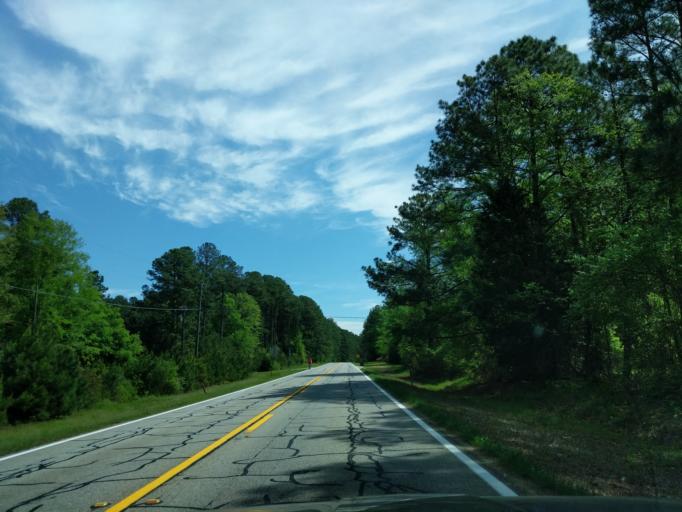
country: US
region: Georgia
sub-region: Columbia County
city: Appling
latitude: 33.6103
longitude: -82.3419
